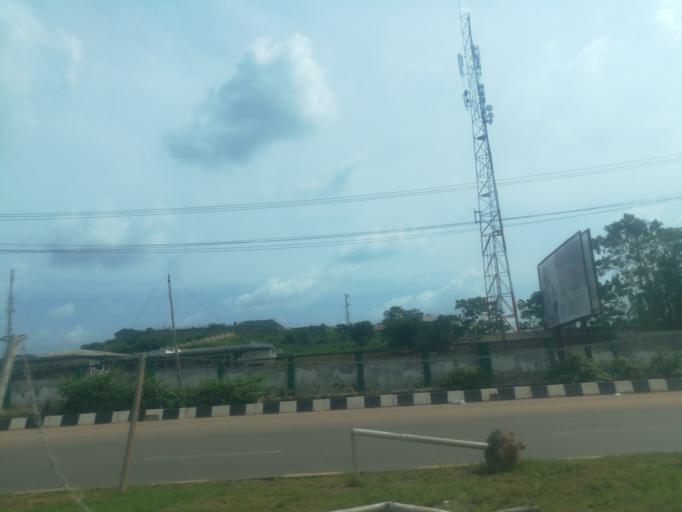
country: NG
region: Ogun
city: Abeokuta
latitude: 7.1317
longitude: 3.3645
